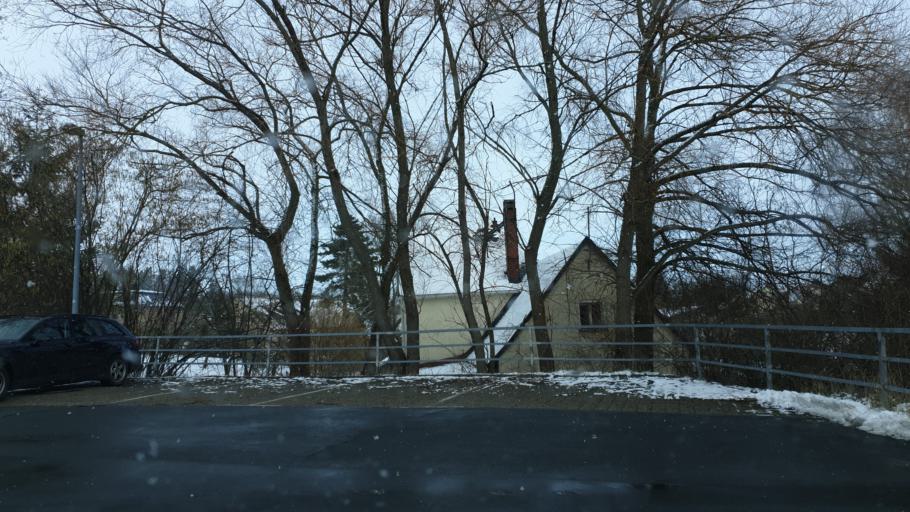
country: DE
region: Saxony
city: Oelsnitz
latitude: 50.4019
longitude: 12.1548
